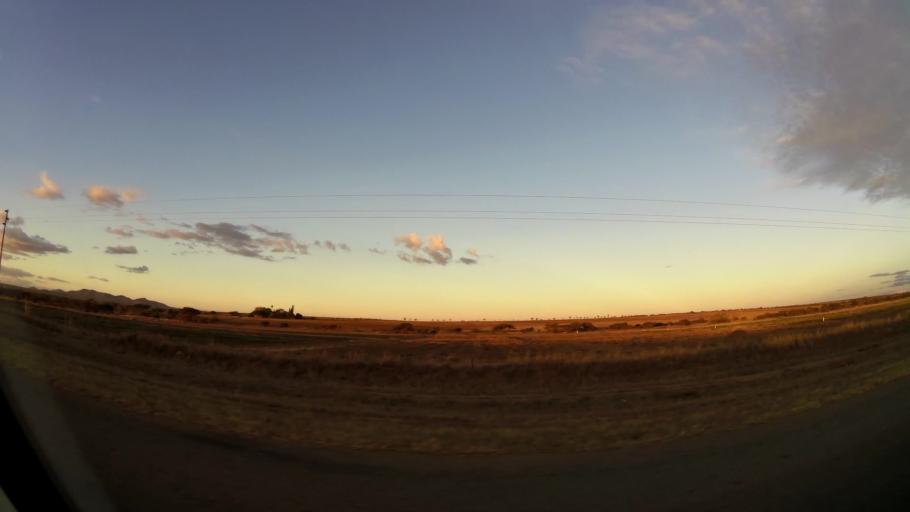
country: ZA
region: Limpopo
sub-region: Capricorn District Municipality
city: Polokwane
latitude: -23.7839
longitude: 29.4753
